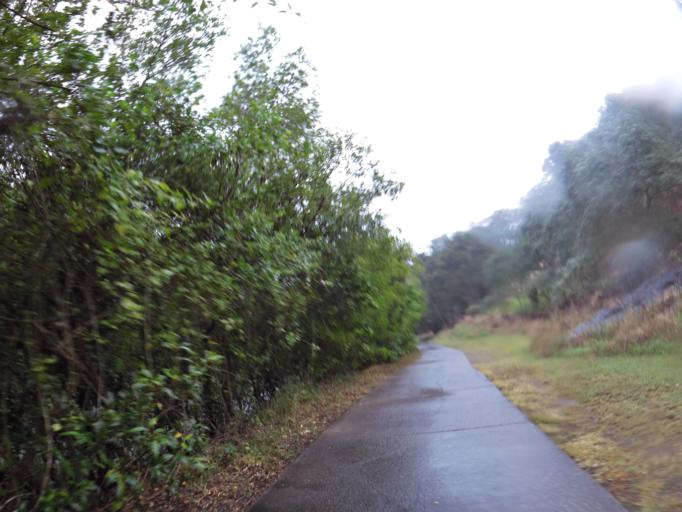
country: AU
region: Queensland
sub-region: Cairns
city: Cairns
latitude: -16.8955
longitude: 145.7529
